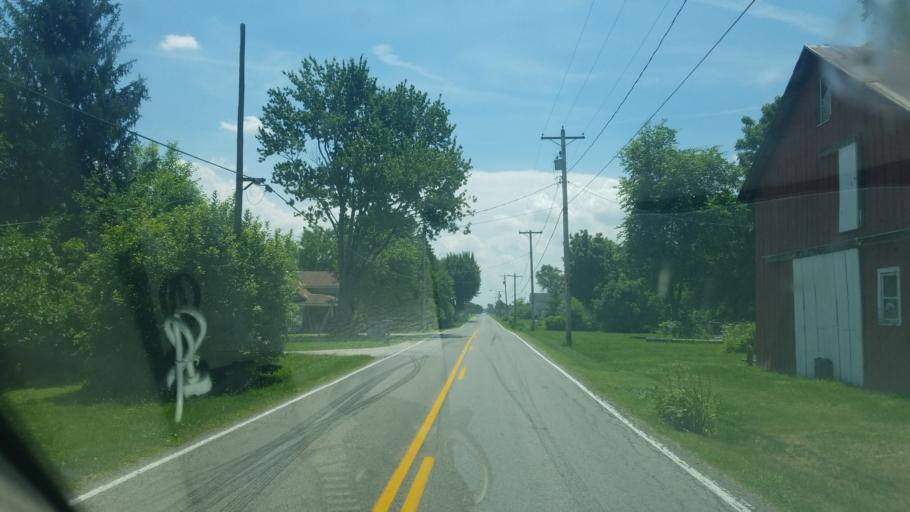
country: US
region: Ohio
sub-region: Hancock County
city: Arlington
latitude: 40.9341
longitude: -83.5945
